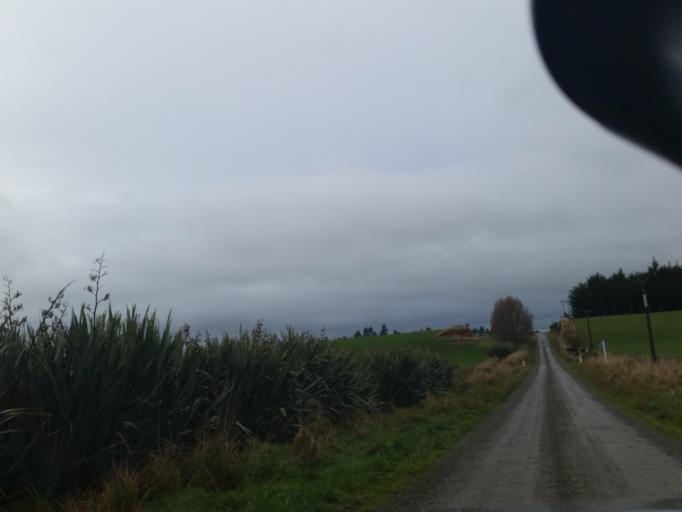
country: NZ
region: Southland
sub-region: Southland District
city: Winton
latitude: -46.2521
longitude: 168.2568
